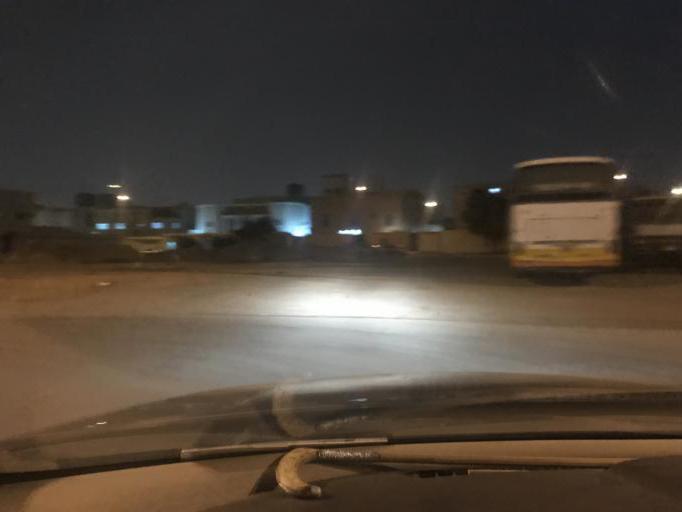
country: SA
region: Ar Riyad
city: Riyadh
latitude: 24.7530
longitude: 46.7766
